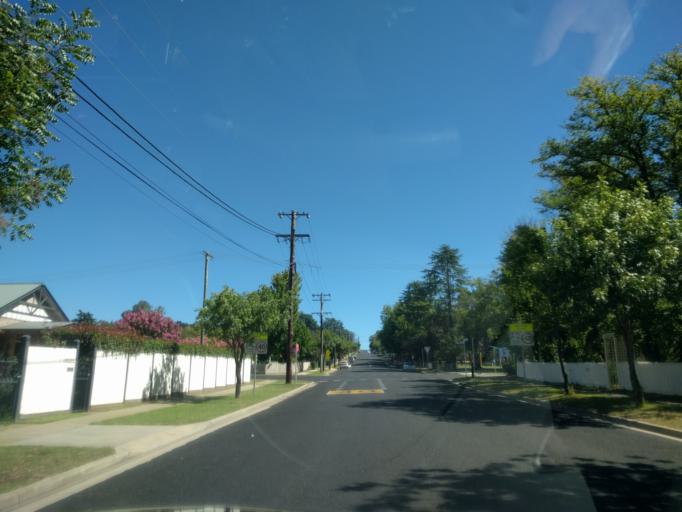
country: AU
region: New South Wales
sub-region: Armidale Dumaresq
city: Armidale
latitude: -30.5183
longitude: 151.6655
